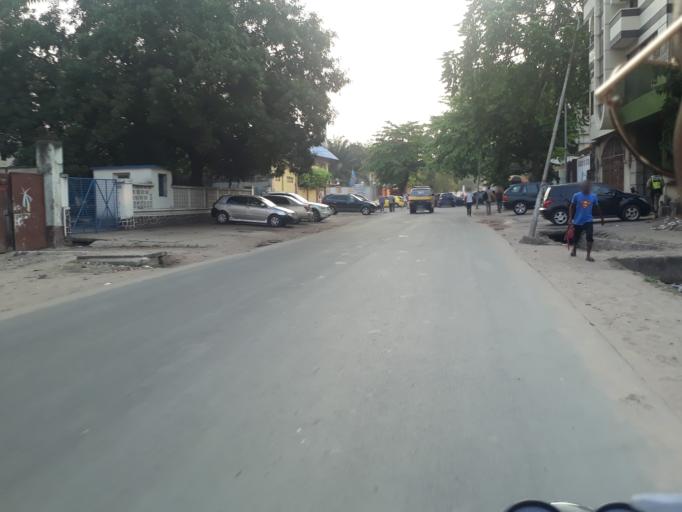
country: CD
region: Kinshasa
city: Kinshasa
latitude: -4.3077
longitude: 15.3025
